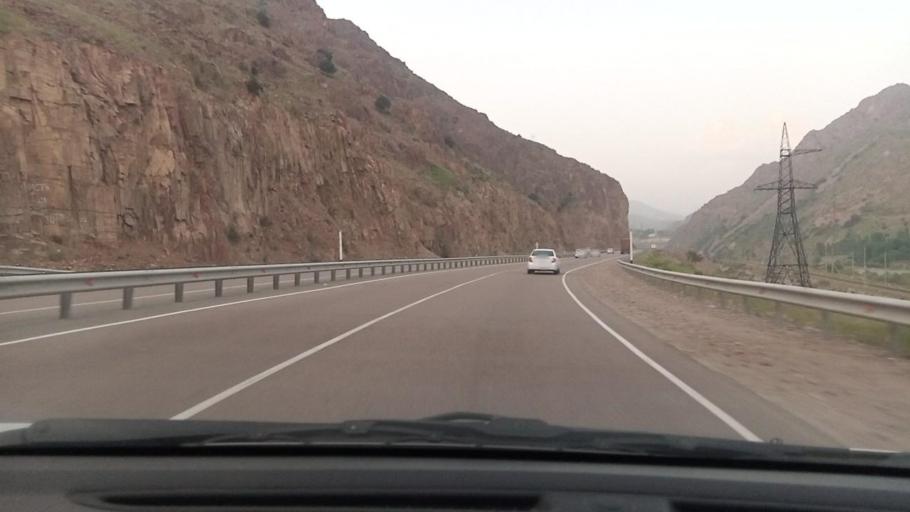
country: UZ
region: Toshkent
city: Angren
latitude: 41.1154
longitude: 70.3407
